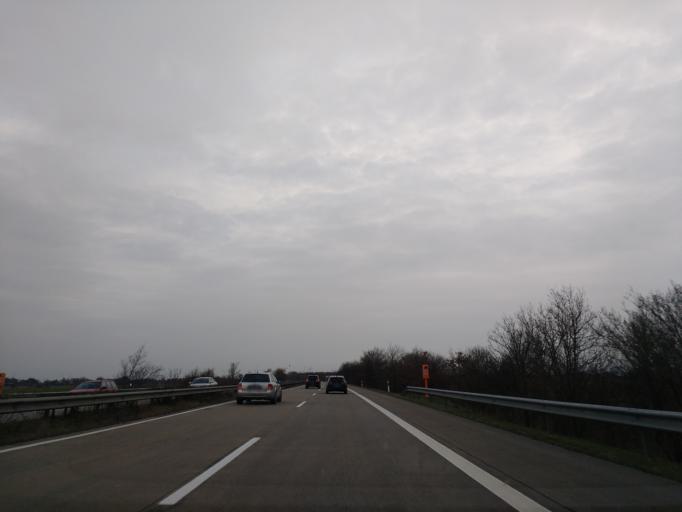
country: DE
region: Lower Saxony
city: Midlum
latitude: 53.7712
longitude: 8.7013
